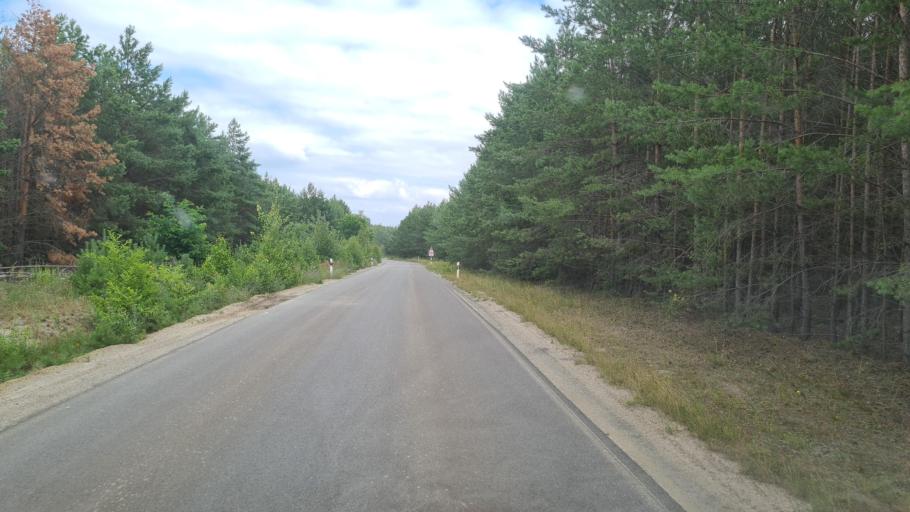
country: DE
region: Brandenburg
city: Neupetershain
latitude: 51.6442
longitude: 14.1054
